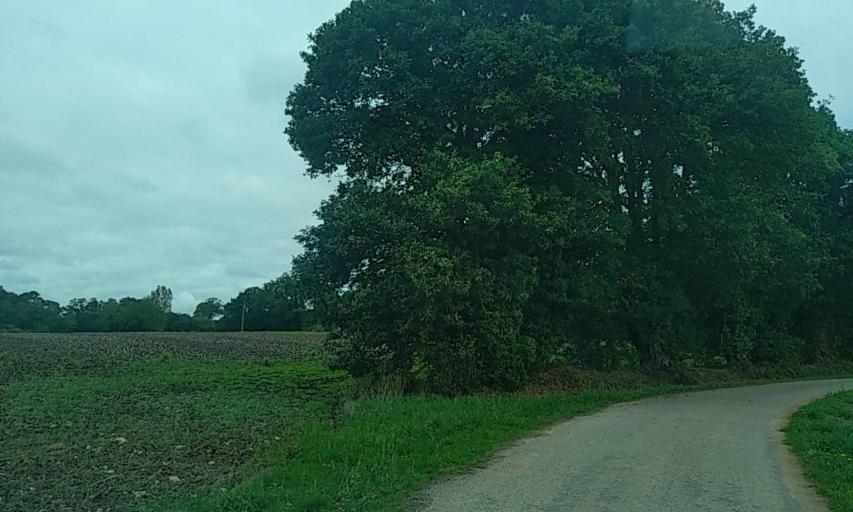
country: FR
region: Brittany
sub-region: Departement du Morbihan
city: Pont-Scorff
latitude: 47.8072
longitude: -3.3843
